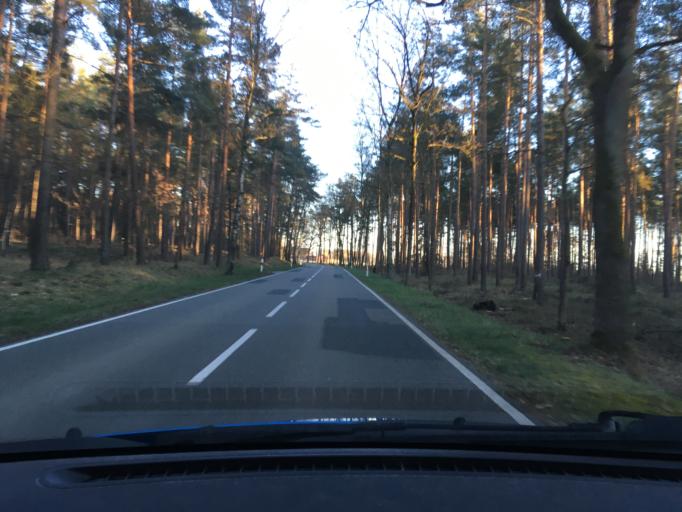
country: DE
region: Lower Saxony
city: Dahlem
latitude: 53.2384
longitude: 10.7517
